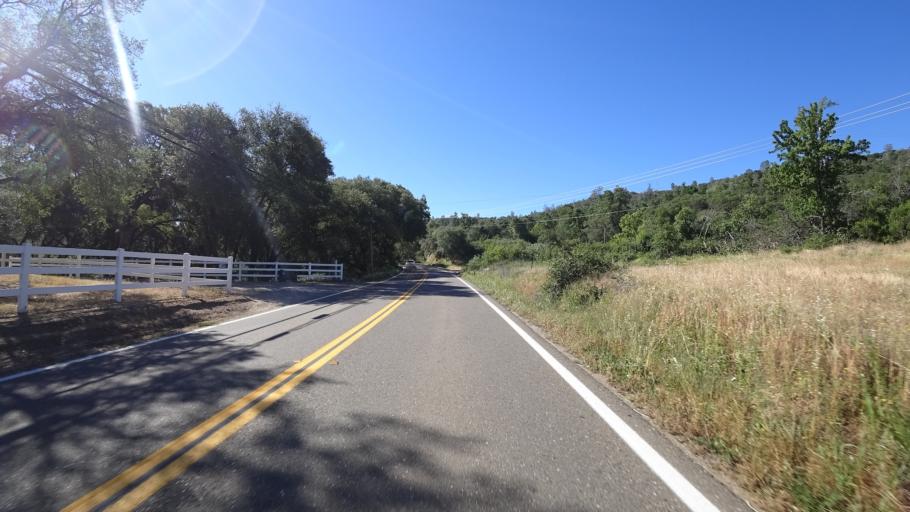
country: US
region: California
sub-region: Placer County
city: Newcastle
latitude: 38.8821
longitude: -121.1729
